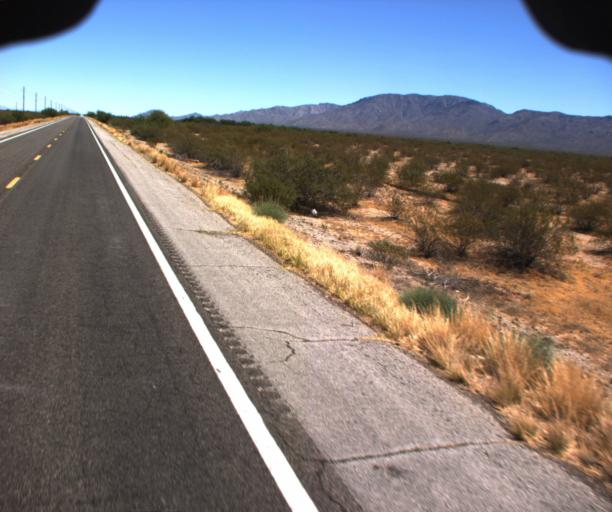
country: US
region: Arizona
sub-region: La Paz County
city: Salome
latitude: 33.8355
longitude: -113.4933
